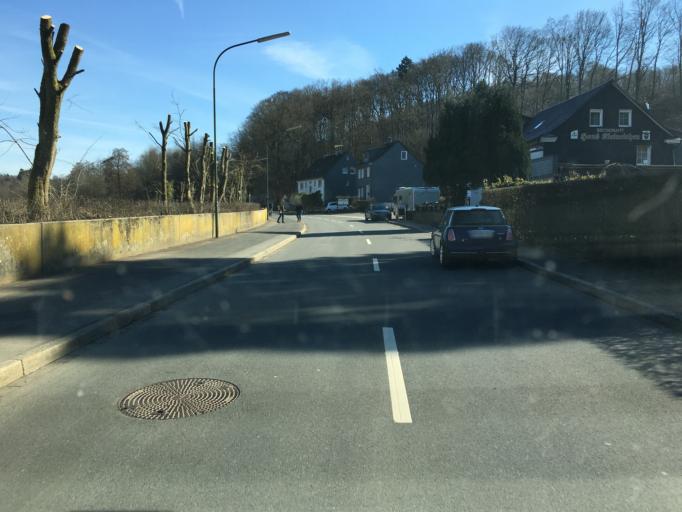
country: DE
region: North Rhine-Westphalia
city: Huckeswagen
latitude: 51.1379
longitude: 7.3556
